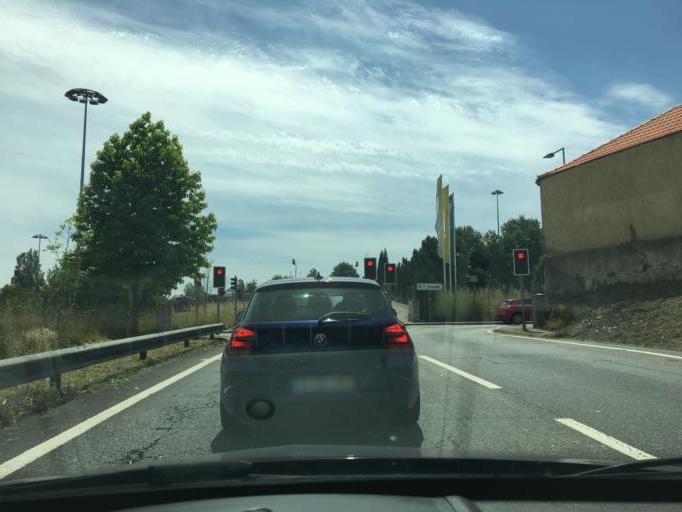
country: PT
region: Porto
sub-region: Porto
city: Porto
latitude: 41.1716
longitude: -8.6061
